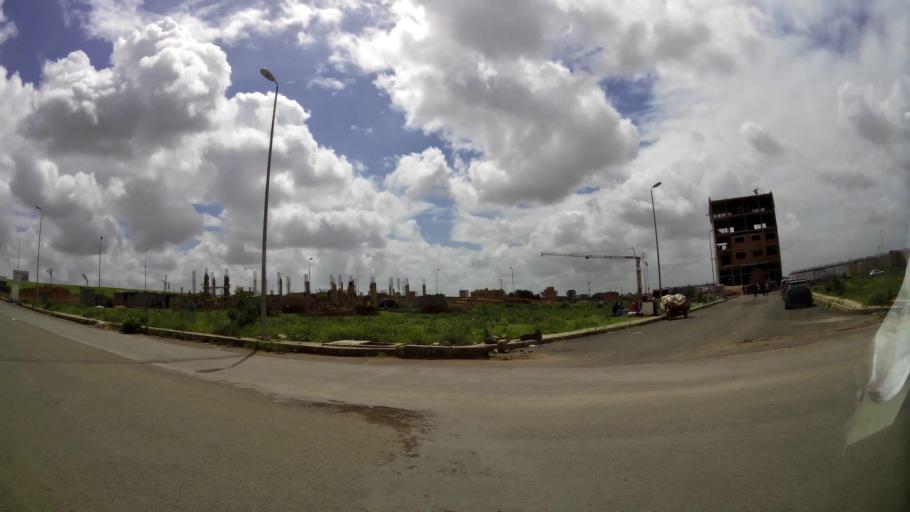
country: MA
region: Grand Casablanca
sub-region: Casablanca
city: Casablanca
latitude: 33.5276
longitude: -7.6027
